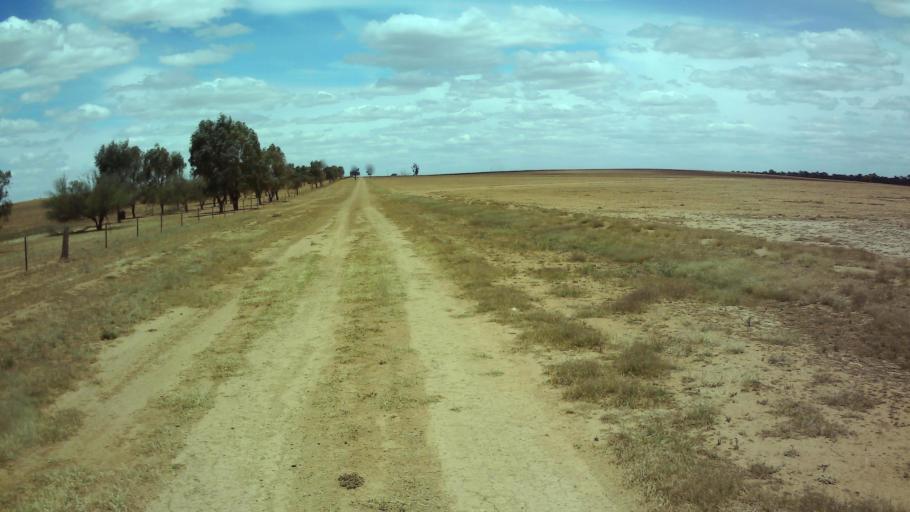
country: AU
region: New South Wales
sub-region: Weddin
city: Grenfell
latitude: -33.8936
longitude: 147.7409
